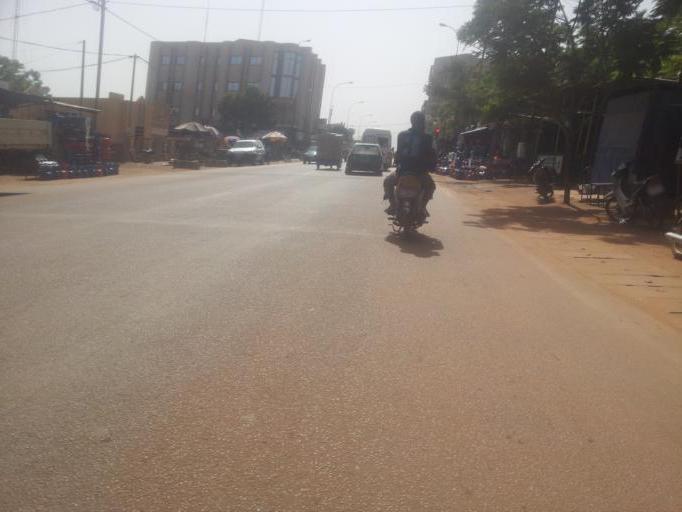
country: BF
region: Centre
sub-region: Kadiogo Province
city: Ouagadougou
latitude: 12.3775
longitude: -1.5331
